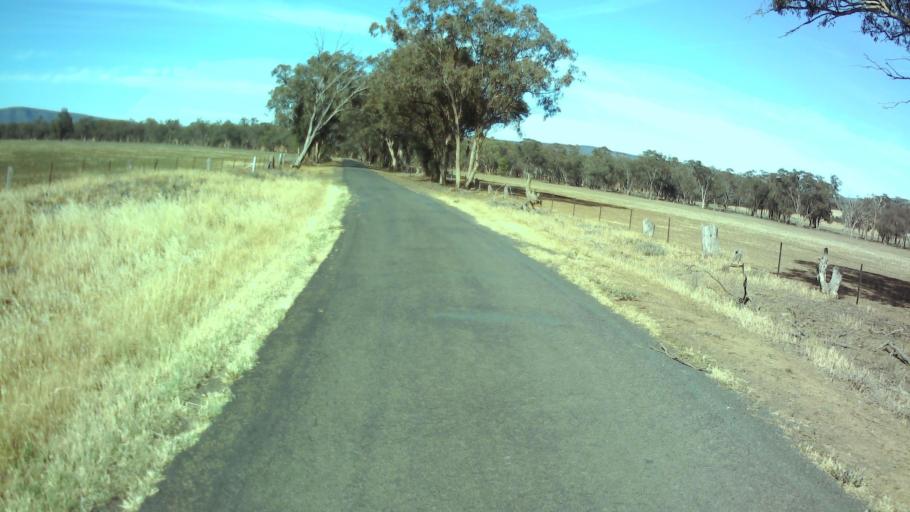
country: AU
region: New South Wales
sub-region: Weddin
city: Grenfell
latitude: -33.9052
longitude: 148.0844
